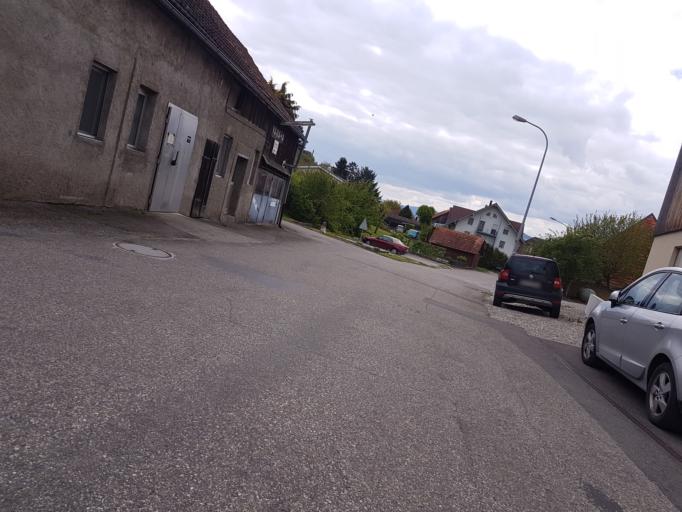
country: CH
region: Bern
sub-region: Seeland District
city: Leuzigen
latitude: 47.1745
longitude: 7.4574
